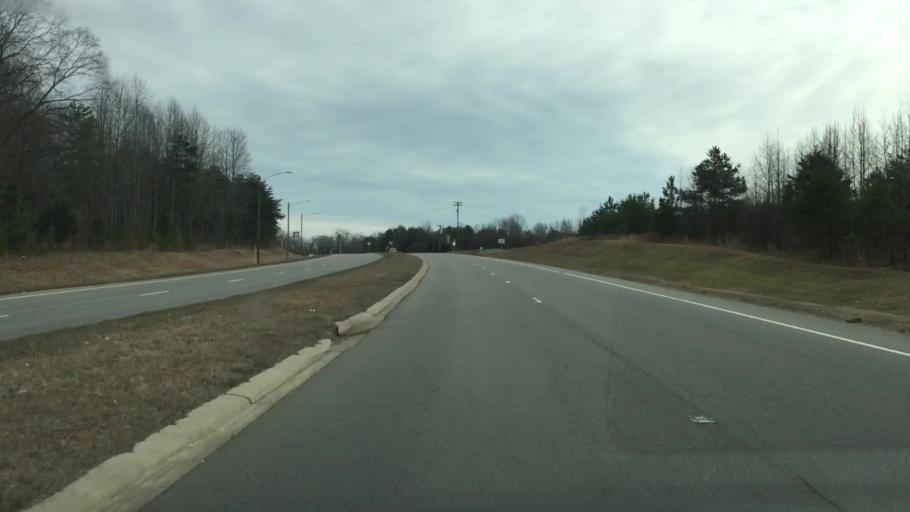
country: US
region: North Carolina
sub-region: Rockingham County
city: Reidsville
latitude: 36.3160
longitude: -79.6772
